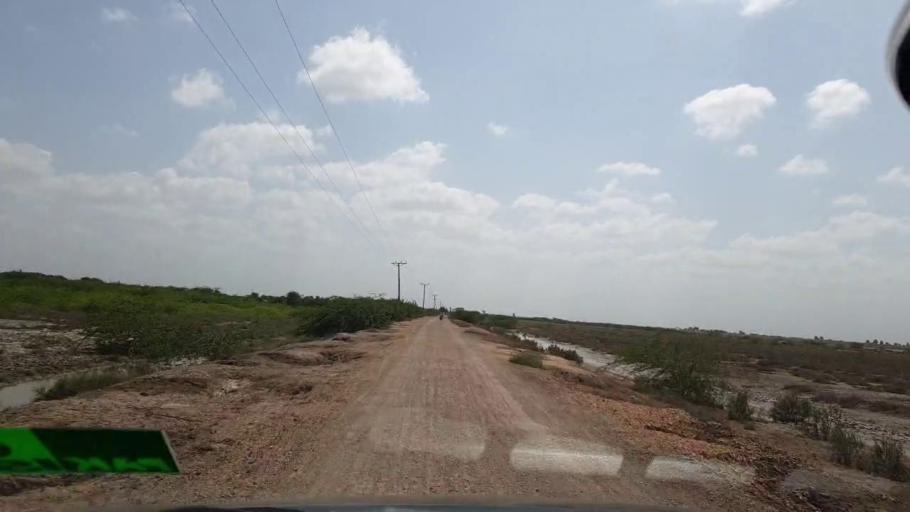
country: PK
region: Sindh
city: Kadhan
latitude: 24.6032
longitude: 69.1852
